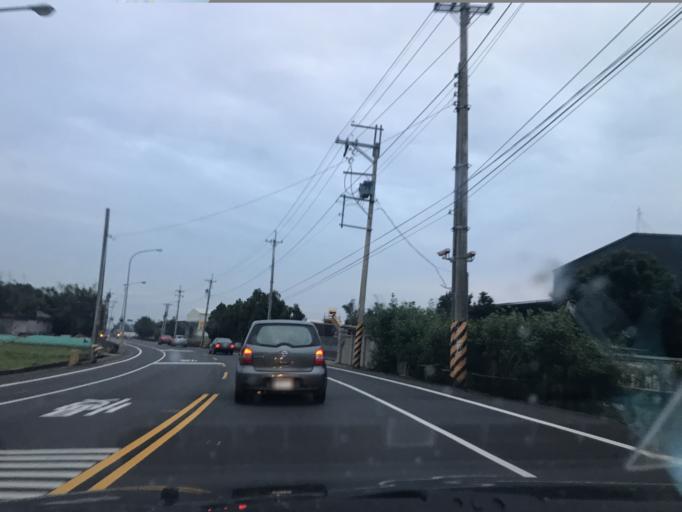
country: TW
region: Taiwan
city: Daxi
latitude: 24.8886
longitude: 121.2238
